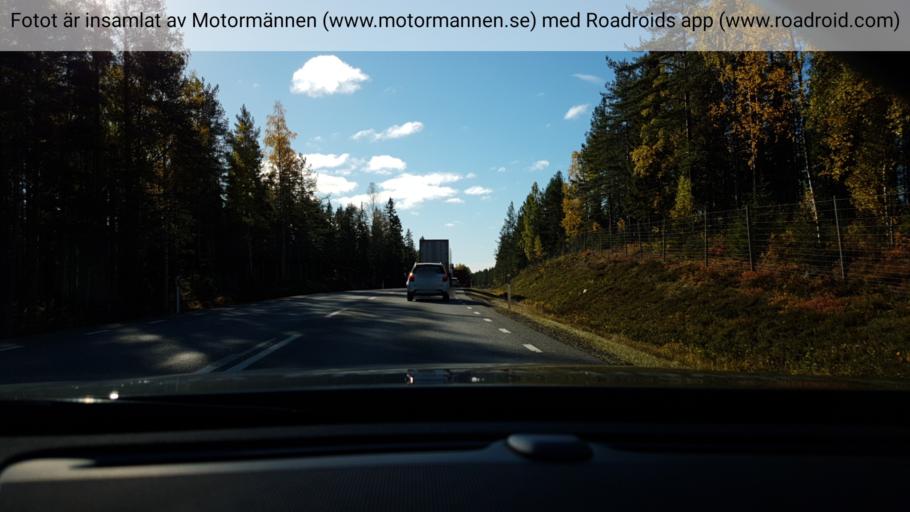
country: SE
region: Vaesterbotten
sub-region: Skelleftea Kommun
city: Burea
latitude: 64.5352
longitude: 21.2587
